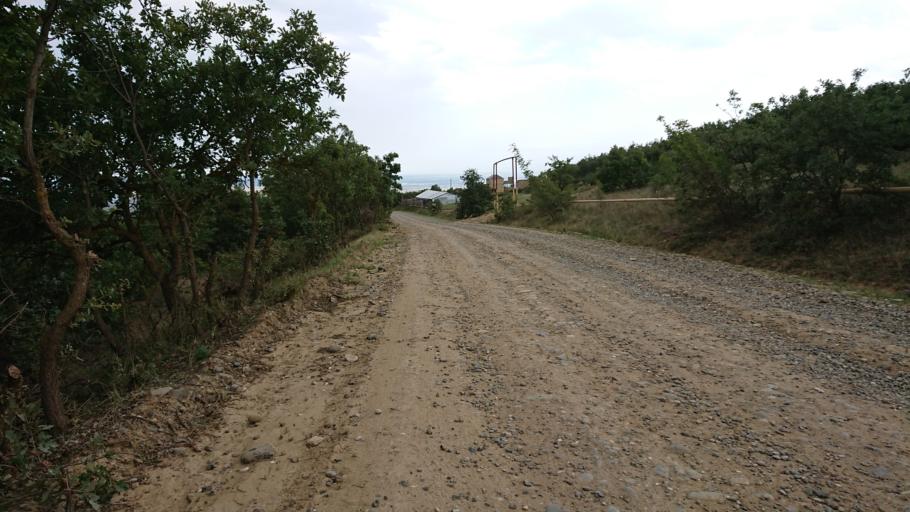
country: RU
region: Dagestan
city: Derbent
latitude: 42.0119
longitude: 48.2708
